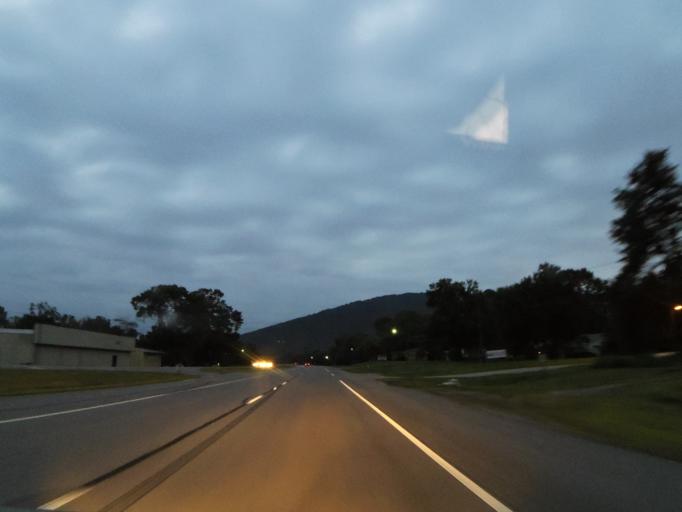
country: US
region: Alabama
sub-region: Madison County
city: New Hope
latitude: 34.6606
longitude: -86.3288
